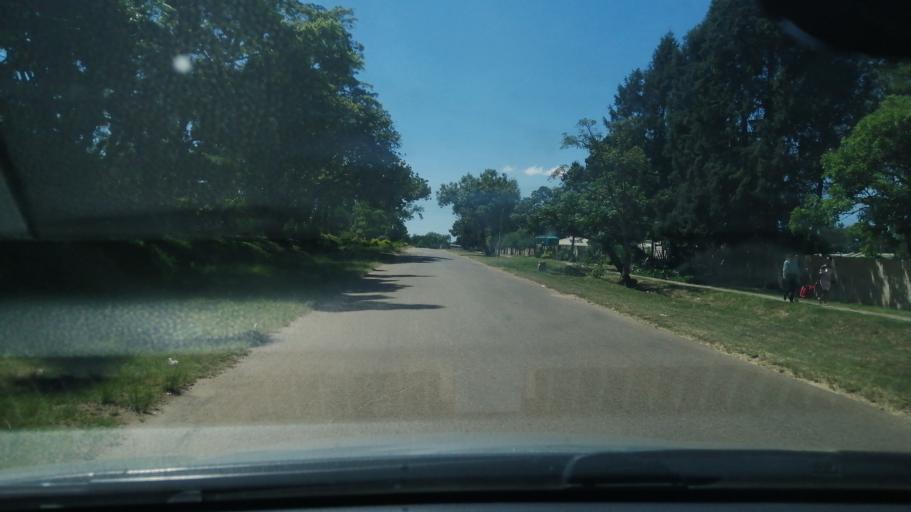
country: ZW
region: Harare
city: Epworth
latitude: -17.8177
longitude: 31.1291
